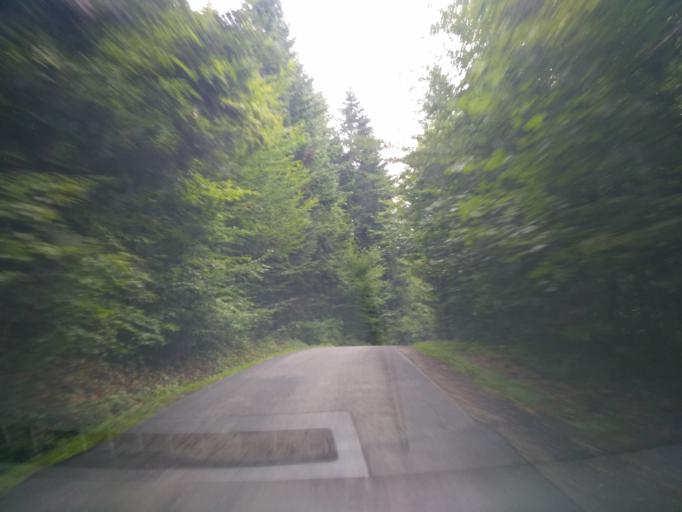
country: PL
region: Subcarpathian Voivodeship
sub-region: Powiat strzyzowski
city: Strzyzow
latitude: 49.8942
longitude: 21.7870
